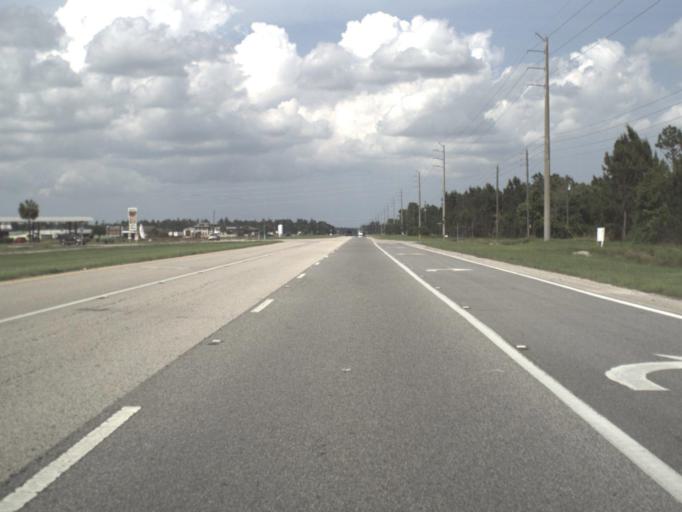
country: US
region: Florida
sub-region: Putnam County
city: East Palatka
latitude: 29.6689
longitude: -81.5903
